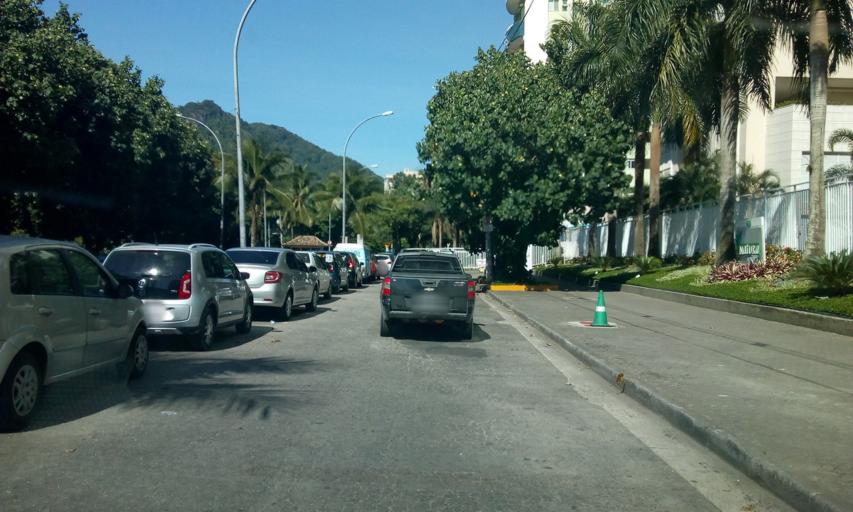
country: BR
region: Rio de Janeiro
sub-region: Nilopolis
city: Nilopolis
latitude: -23.0229
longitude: -43.4882
